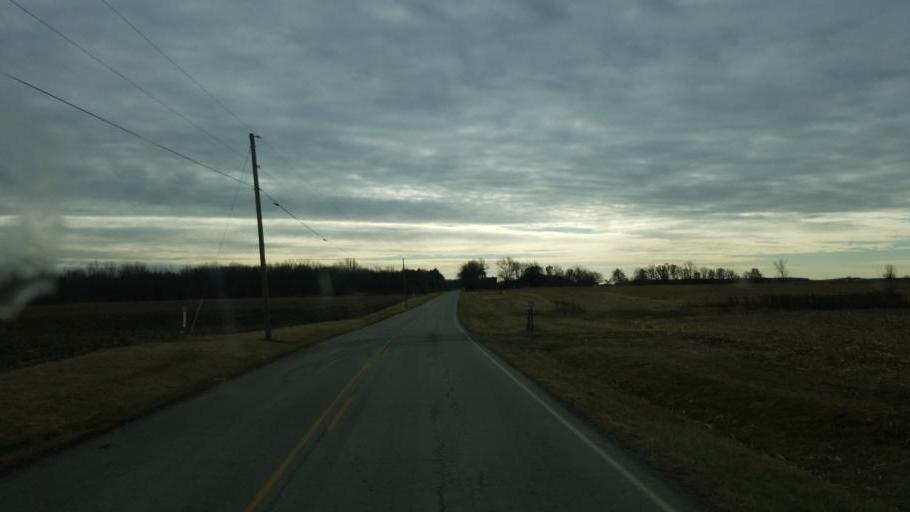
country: US
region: Ohio
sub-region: Wyandot County
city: Upper Sandusky
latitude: 40.7076
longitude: -83.2488
